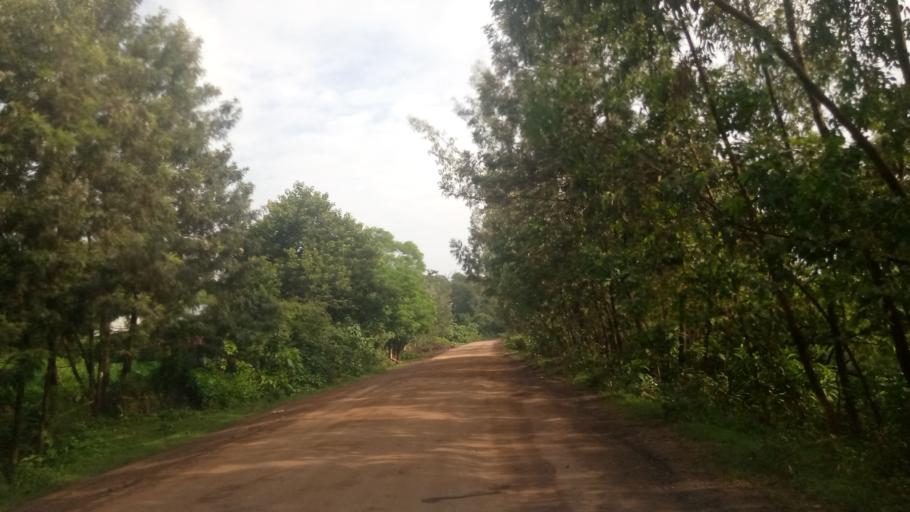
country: ET
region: Oromiya
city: Agaro
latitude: 7.8444
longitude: 36.6587
